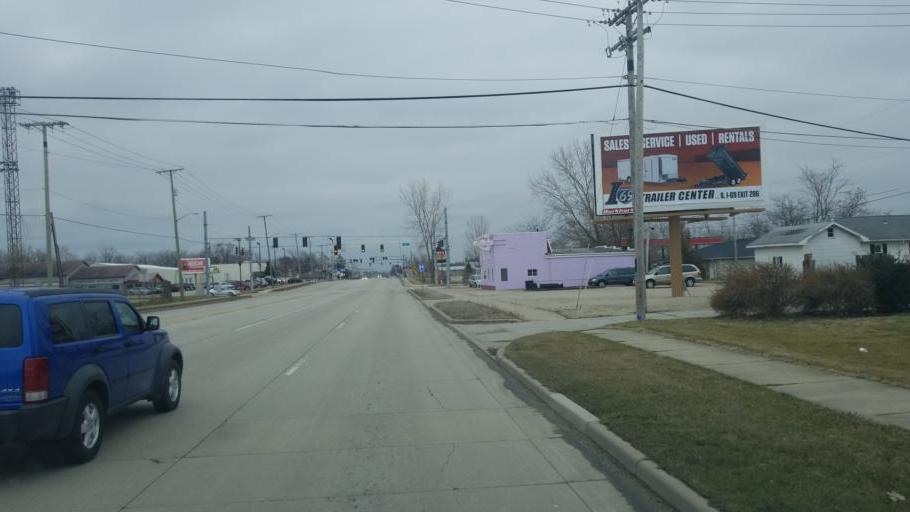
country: US
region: Indiana
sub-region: Adams County
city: Decatur
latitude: 40.8279
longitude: -84.9377
